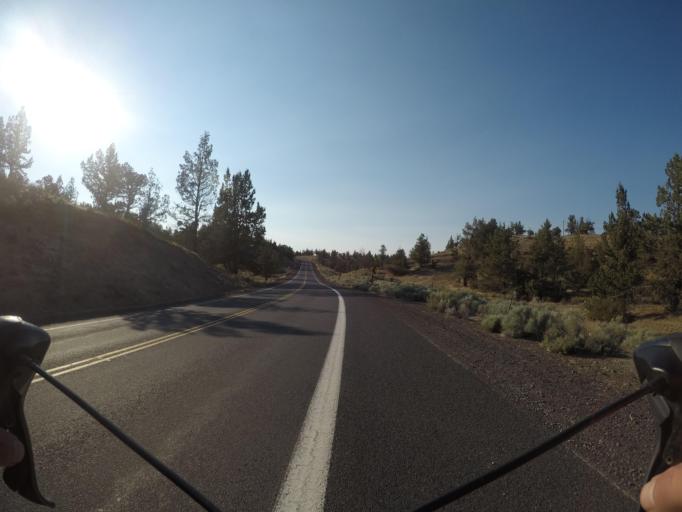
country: US
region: Oregon
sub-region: Deschutes County
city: Redmond
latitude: 44.2712
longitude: -121.2597
